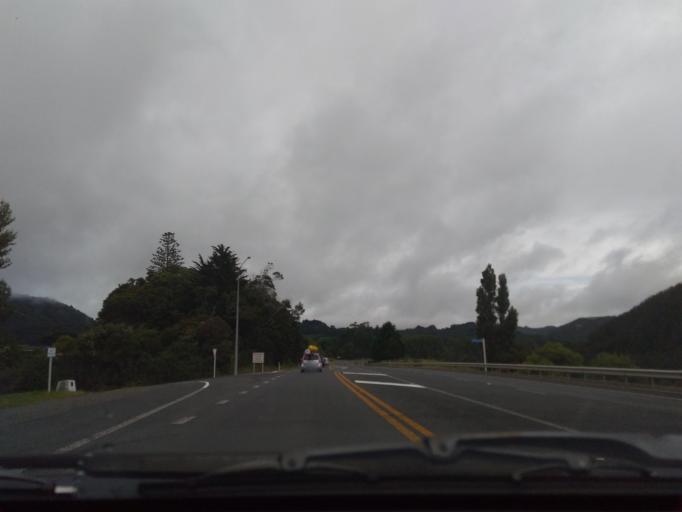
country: NZ
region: Auckland
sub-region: Auckland
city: Wellsford
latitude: -36.1375
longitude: 174.4304
